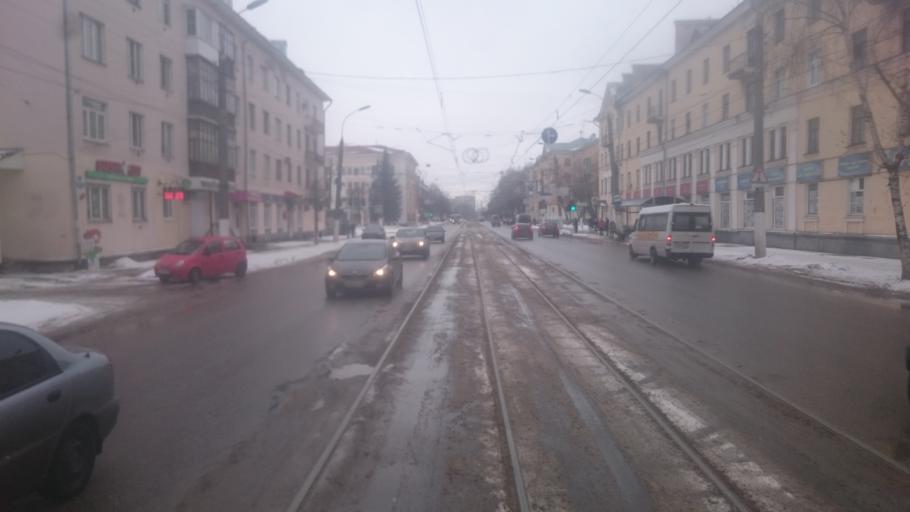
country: RU
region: Tverskaya
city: Tver
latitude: 56.8677
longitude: 35.9023
